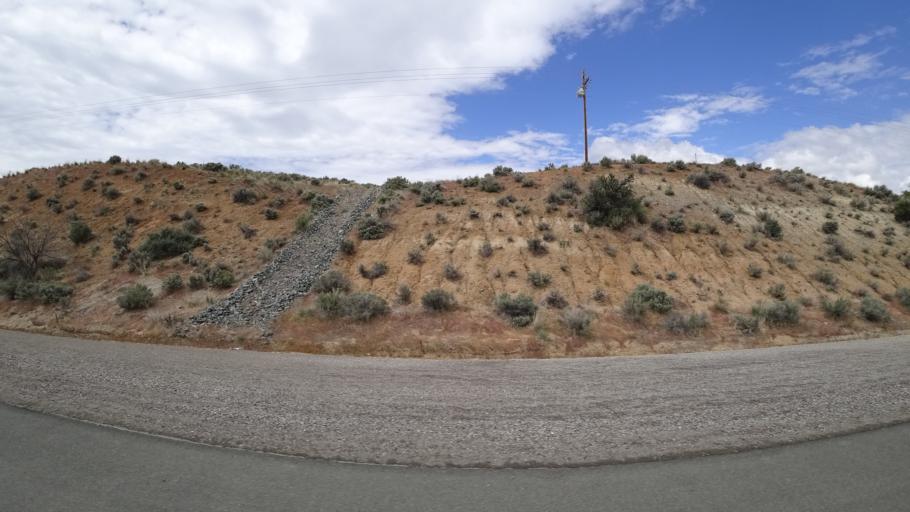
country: US
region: Nevada
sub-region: Douglas County
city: Indian Hills
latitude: 39.0846
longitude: -119.7768
